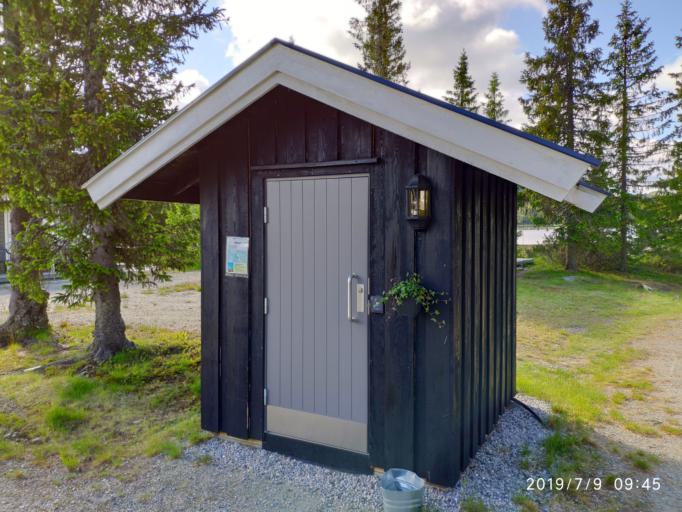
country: NO
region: Buskerud
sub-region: Nes
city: Nesbyen
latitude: 60.3403
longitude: 9.1841
